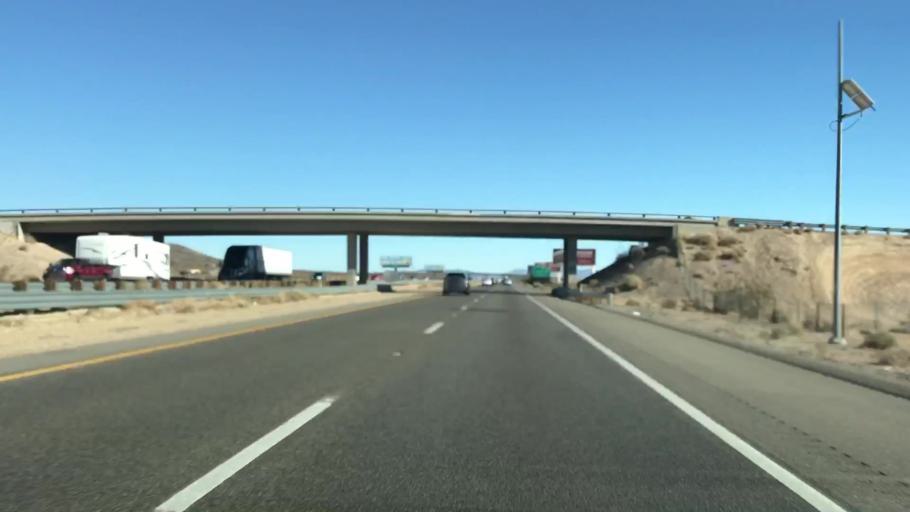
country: US
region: California
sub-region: San Bernardino County
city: Barstow
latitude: 34.9110
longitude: -116.8212
